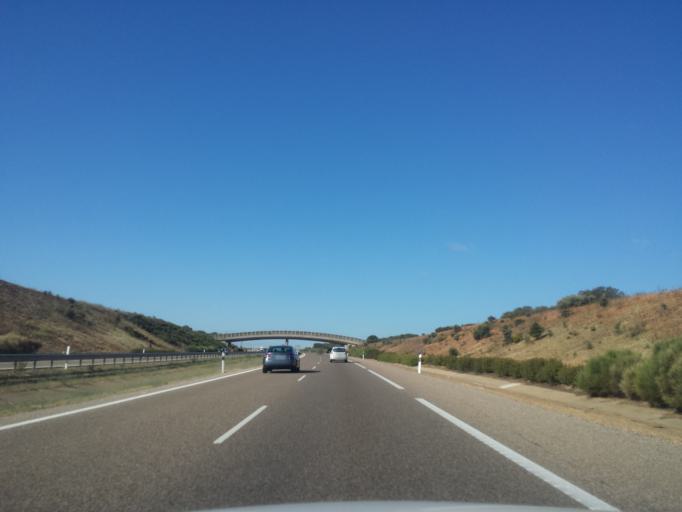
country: ES
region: Castille and Leon
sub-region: Provincia de Leon
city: Villamandos
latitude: 42.1848
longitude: -5.6237
